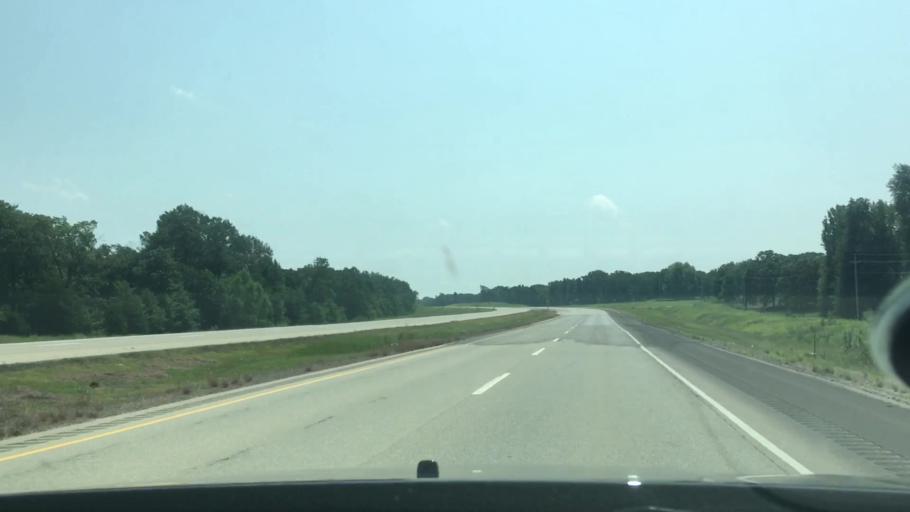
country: US
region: Oklahoma
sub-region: Atoka County
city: Atoka
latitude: 34.3186
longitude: -96.0345
